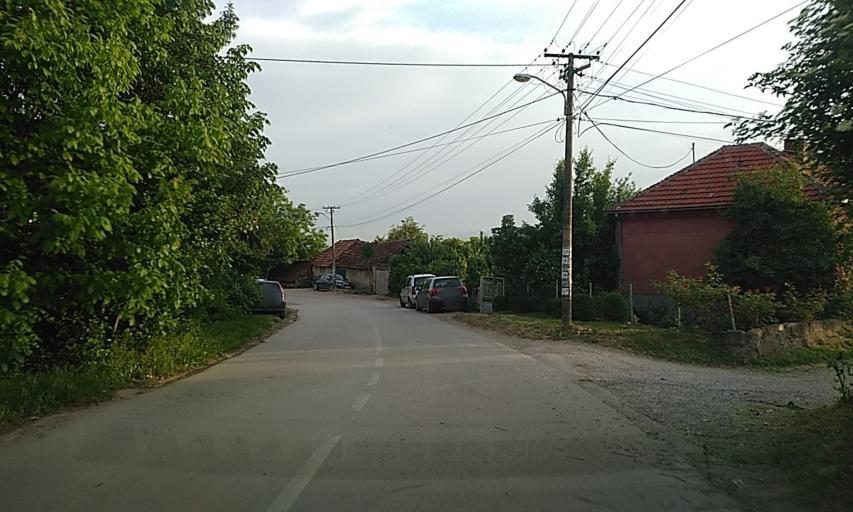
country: RS
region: Central Serbia
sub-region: Nisavski Okrug
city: Nis
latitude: 43.2944
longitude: 21.8656
